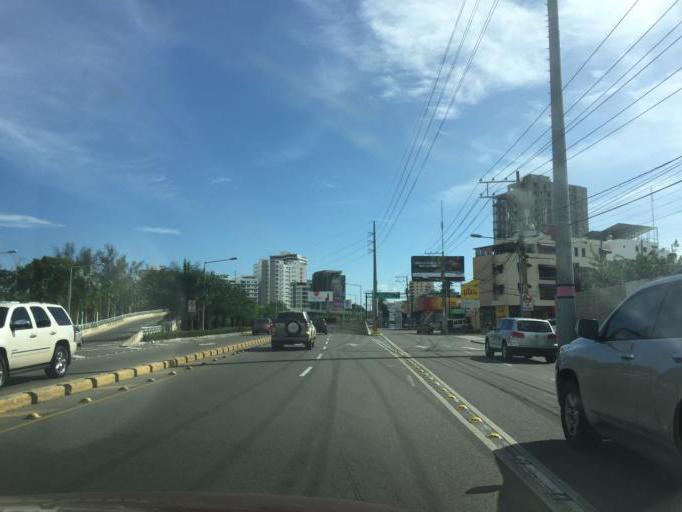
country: DO
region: Nacional
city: La Julia
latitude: 18.4752
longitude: -69.9204
